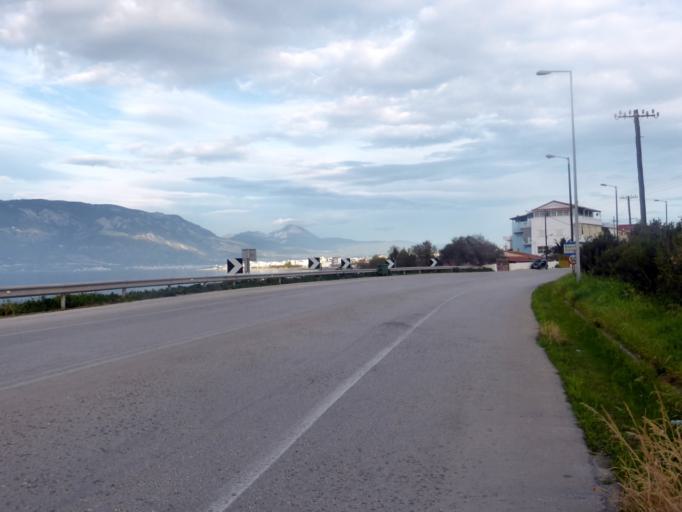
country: GR
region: Peloponnese
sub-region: Nomos Korinthias
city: Arkhaia Korinthos
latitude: 37.9334
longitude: 22.9052
